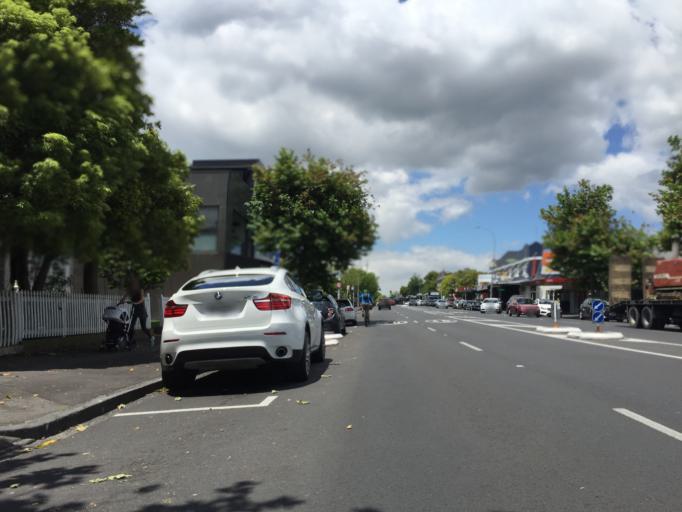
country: NZ
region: Auckland
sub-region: Auckland
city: Auckland
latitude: -36.8511
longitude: 174.7447
